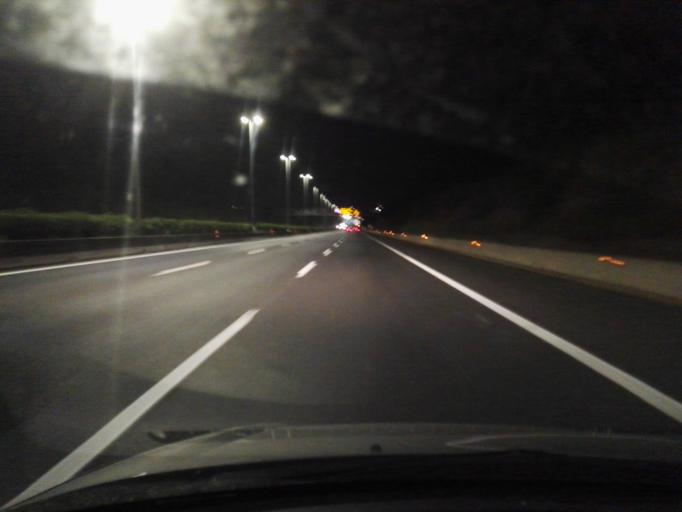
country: IT
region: Latium
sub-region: Citta metropolitana di Roma Capitale
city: Selcetta
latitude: 41.7986
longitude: 12.4731
